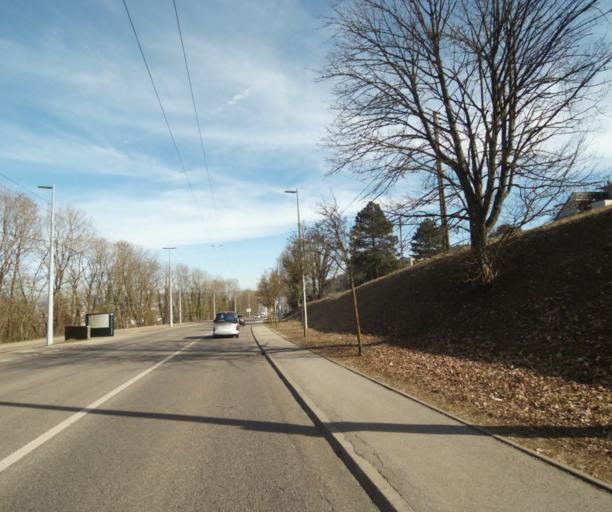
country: FR
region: Lorraine
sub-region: Departement de Meurthe-et-Moselle
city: Villers-les-Nancy
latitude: 48.6574
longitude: 6.1557
